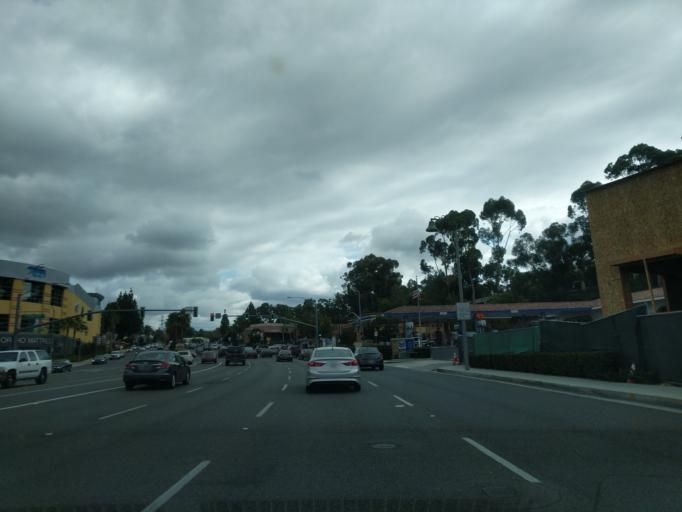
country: US
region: California
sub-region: Orange County
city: Ladera Ranch
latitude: 33.5596
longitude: -117.6716
